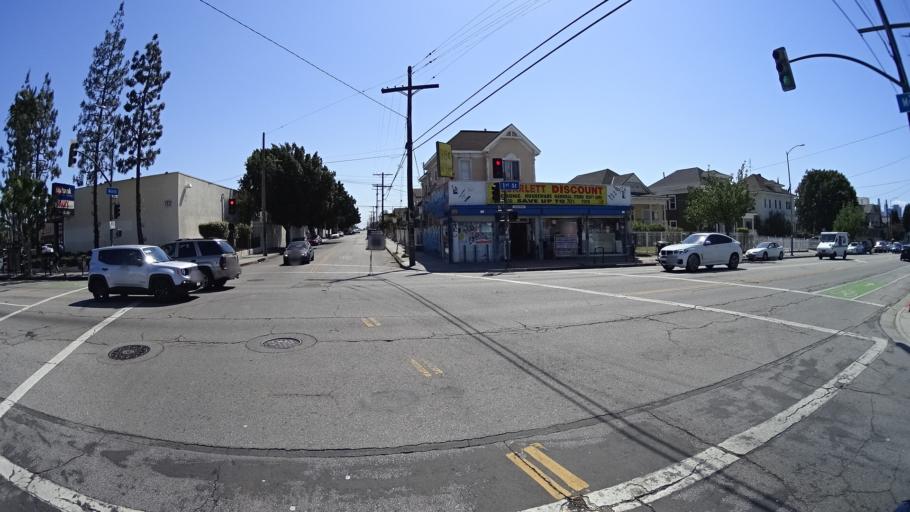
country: US
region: California
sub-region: Los Angeles County
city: Boyle Heights
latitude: 34.0421
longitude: -118.2060
